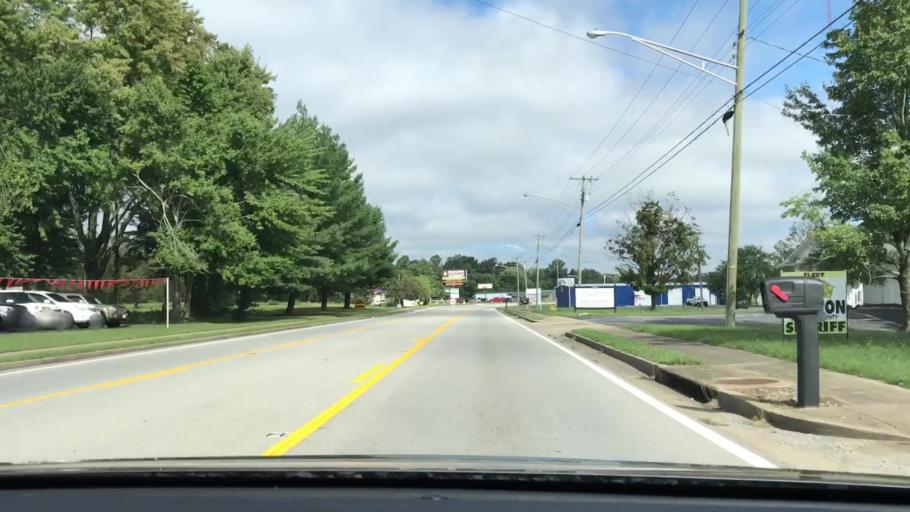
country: US
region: Kentucky
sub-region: Russell County
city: Russell Springs
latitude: 37.0252
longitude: -85.0770
